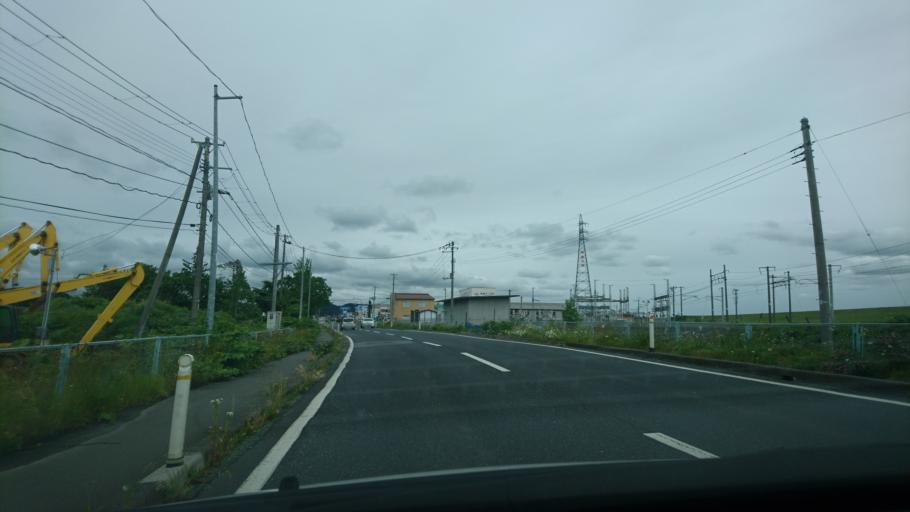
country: JP
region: Iwate
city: Ichinoseki
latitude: 38.9617
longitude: 141.1276
